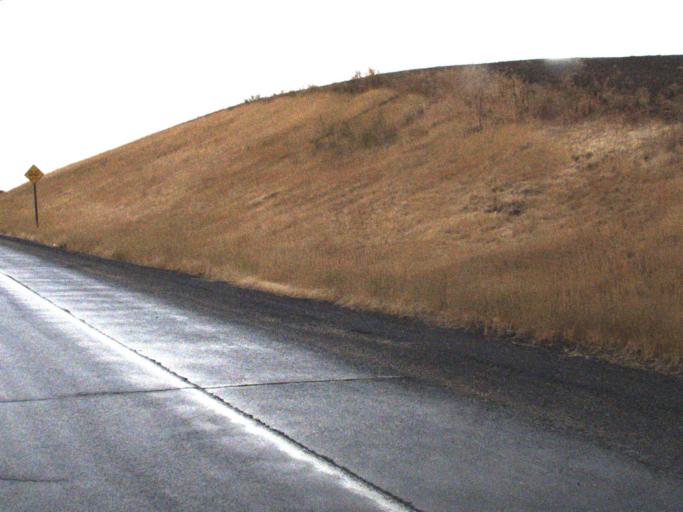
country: US
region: Washington
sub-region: Whitman County
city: Colfax
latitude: 47.1939
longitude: -117.3706
